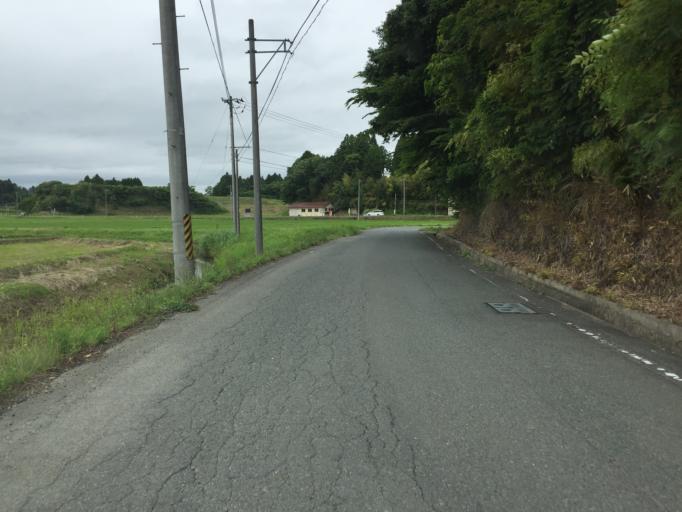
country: JP
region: Fukushima
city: Namie
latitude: 37.7392
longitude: 140.9736
